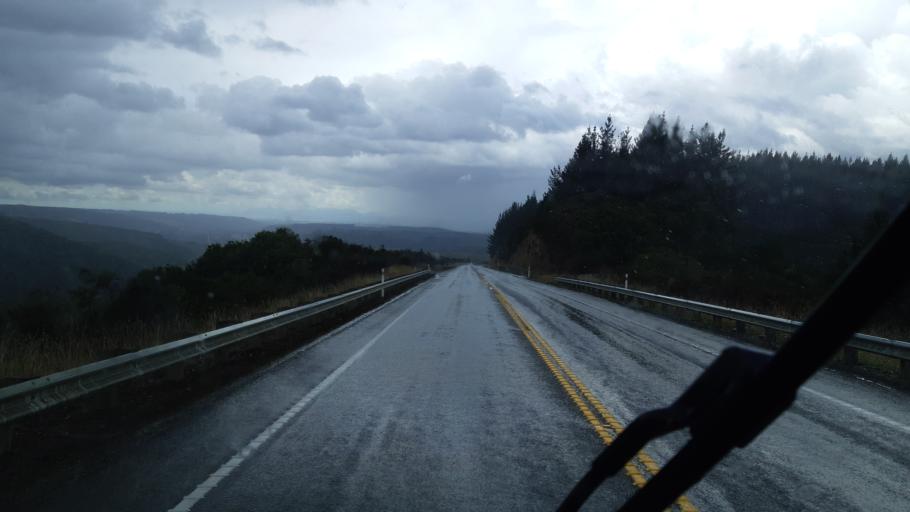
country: NZ
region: Tasman
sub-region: Tasman District
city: Wakefield
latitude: -41.4804
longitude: 172.9154
